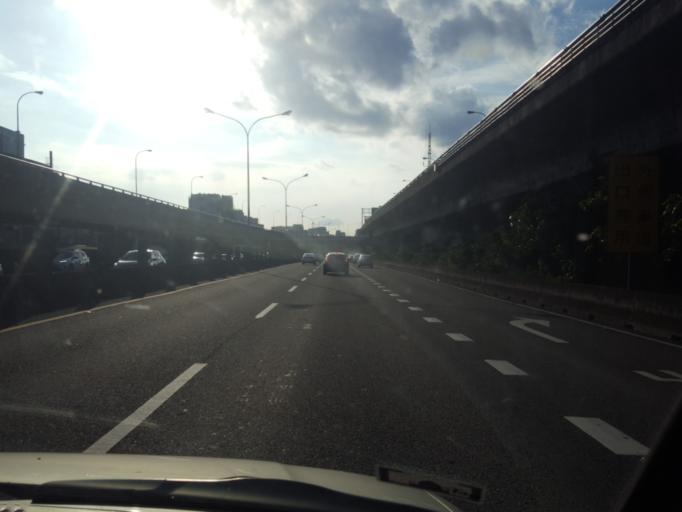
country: TW
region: Taipei
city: Taipei
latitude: 25.0642
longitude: 121.6018
